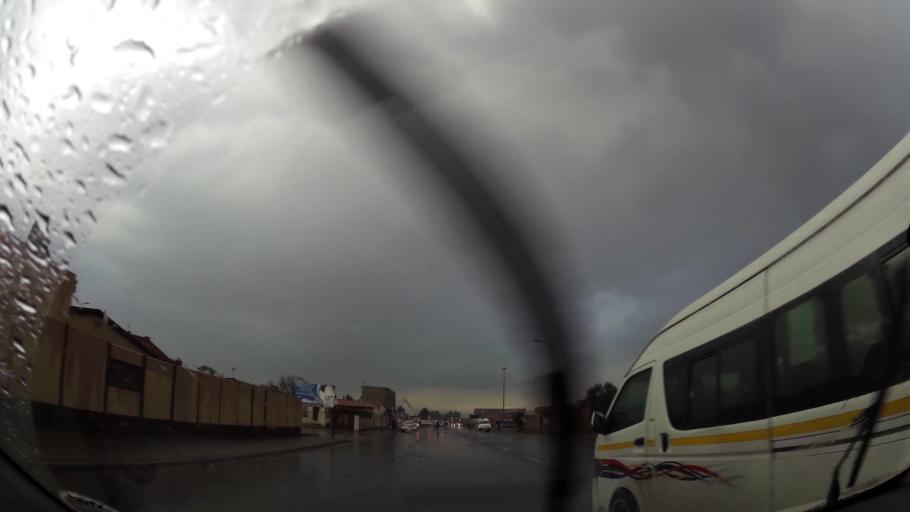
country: ZA
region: Gauteng
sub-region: Ekurhuleni Metropolitan Municipality
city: Germiston
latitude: -26.3465
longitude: 28.1358
